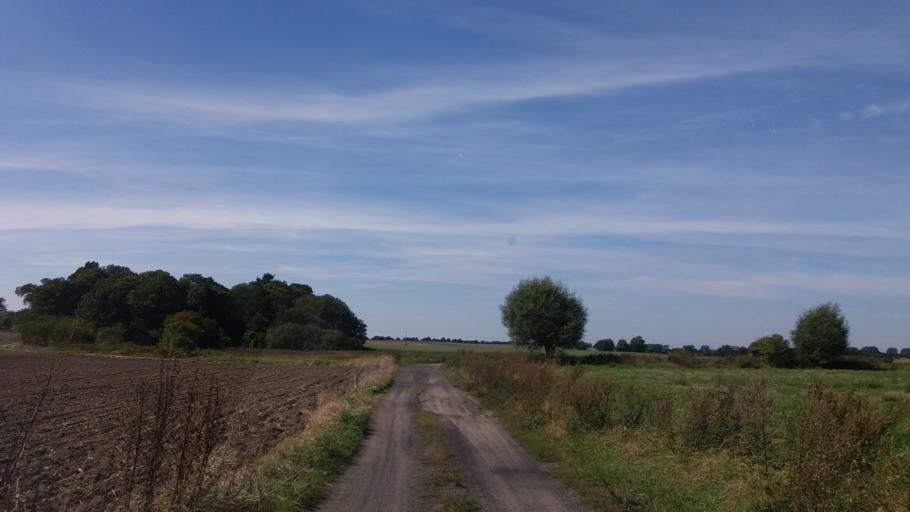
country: PL
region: West Pomeranian Voivodeship
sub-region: Powiat choszczenski
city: Choszczno
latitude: 53.1378
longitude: 15.4036
